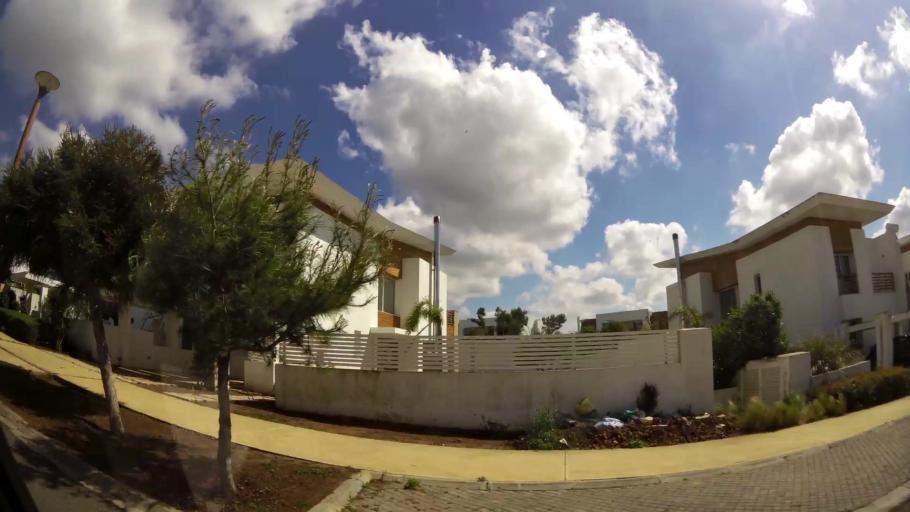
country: MA
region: Grand Casablanca
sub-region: Nouaceur
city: Bouskoura
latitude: 33.4840
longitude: -7.5905
